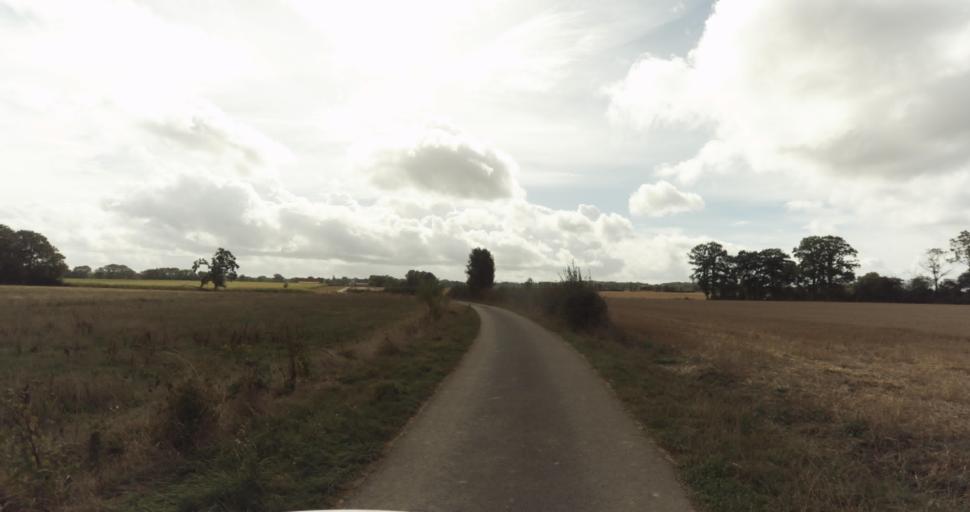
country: FR
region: Lower Normandy
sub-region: Departement de l'Orne
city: Sainte-Gauburge-Sainte-Colombe
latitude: 48.8263
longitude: 0.4079
